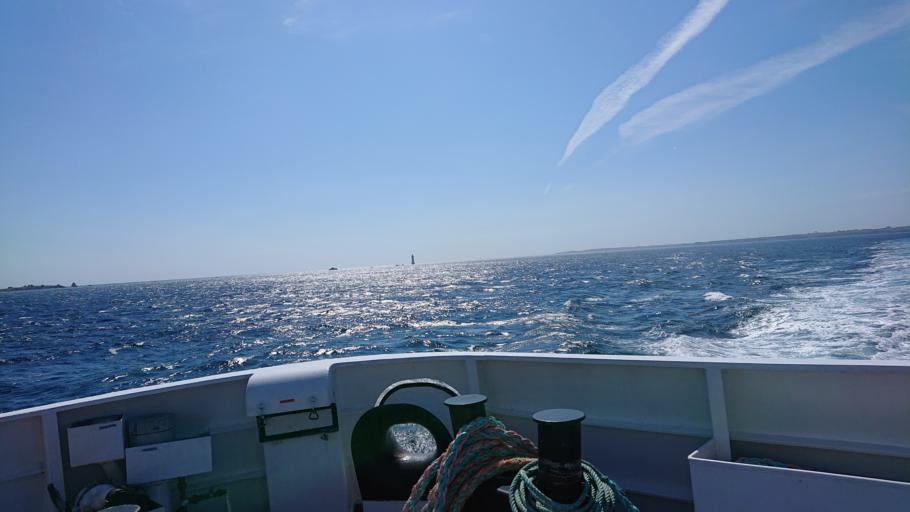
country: FR
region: Brittany
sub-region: Departement du Finistere
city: Lampaul-Plouarzel
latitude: 48.4452
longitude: -4.9939
